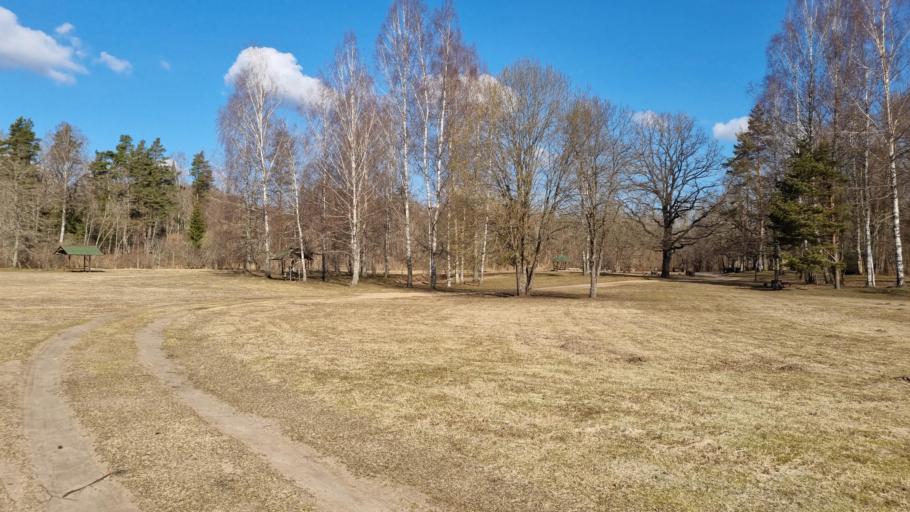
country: LV
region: Talsu Rajons
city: Sabile
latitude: 57.0687
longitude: 22.5282
